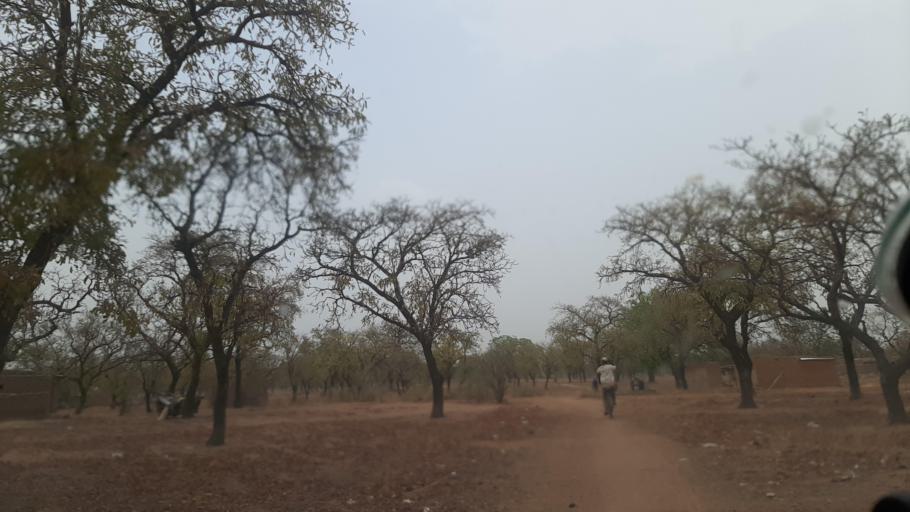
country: BF
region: Boucle du Mouhoun
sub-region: Province des Banwa
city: Salanso
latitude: 11.8691
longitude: -4.4467
